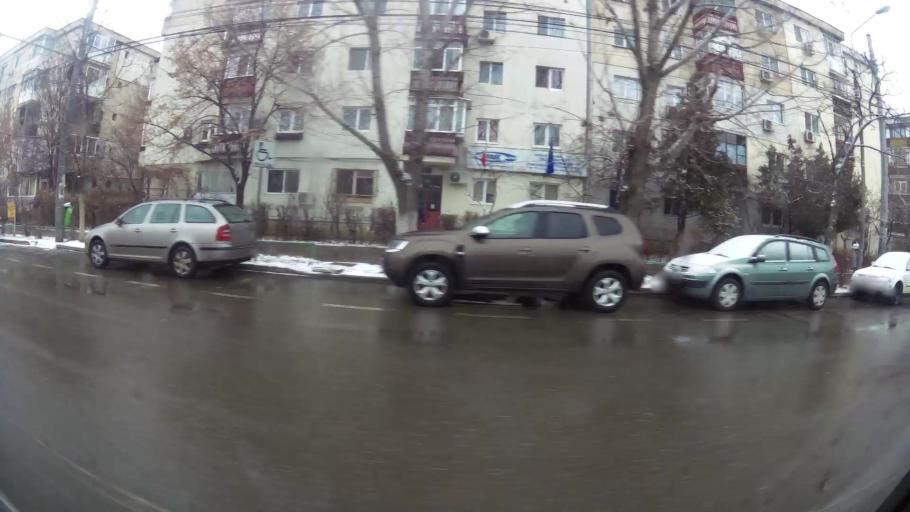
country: RO
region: Prahova
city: Ploiesti
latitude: 44.9399
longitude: 26.0036
